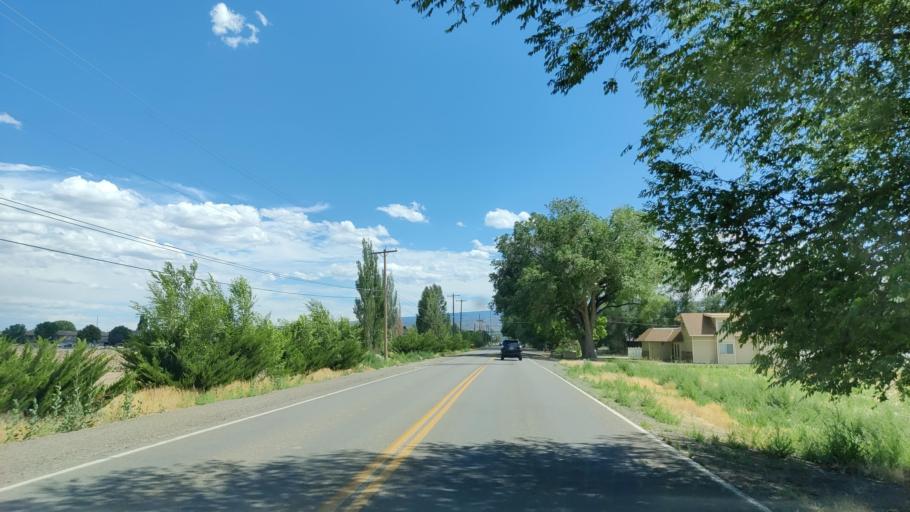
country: US
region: Colorado
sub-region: Mesa County
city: Redlands
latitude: 39.1051
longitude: -108.5988
